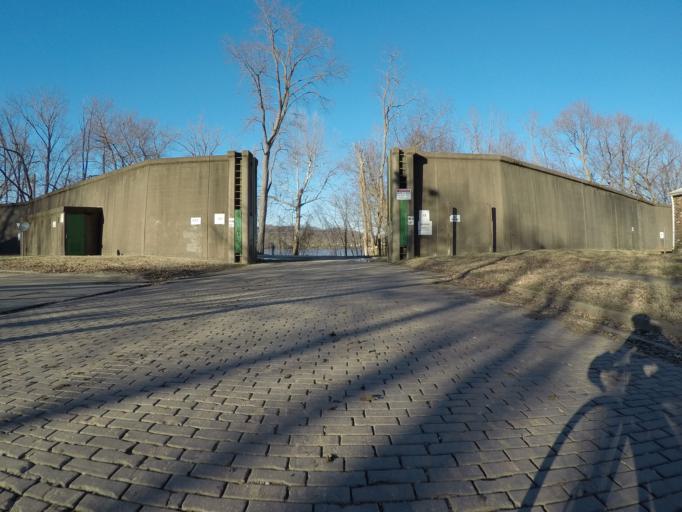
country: US
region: West Virginia
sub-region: Cabell County
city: Huntington
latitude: 38.4303
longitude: -82.3856
